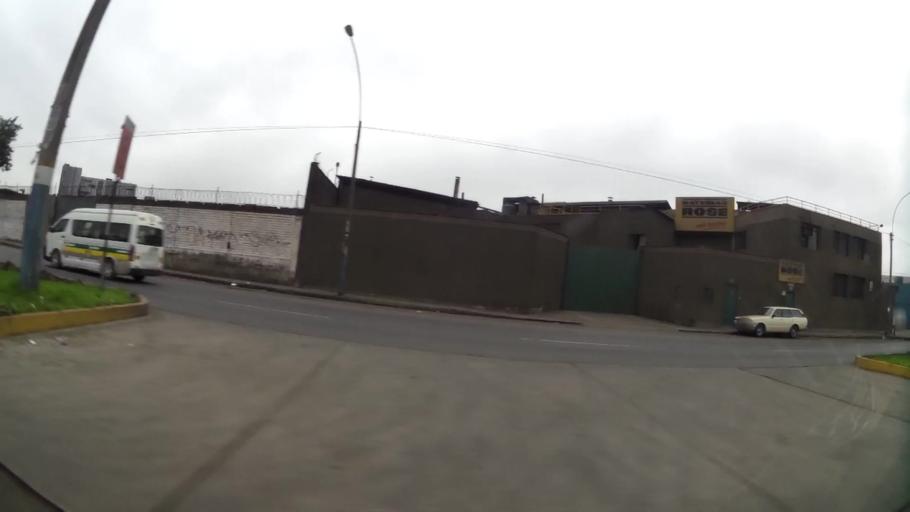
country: PE
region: Lima
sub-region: Lima
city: San Luis
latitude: -12.0645
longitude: -76.9785
